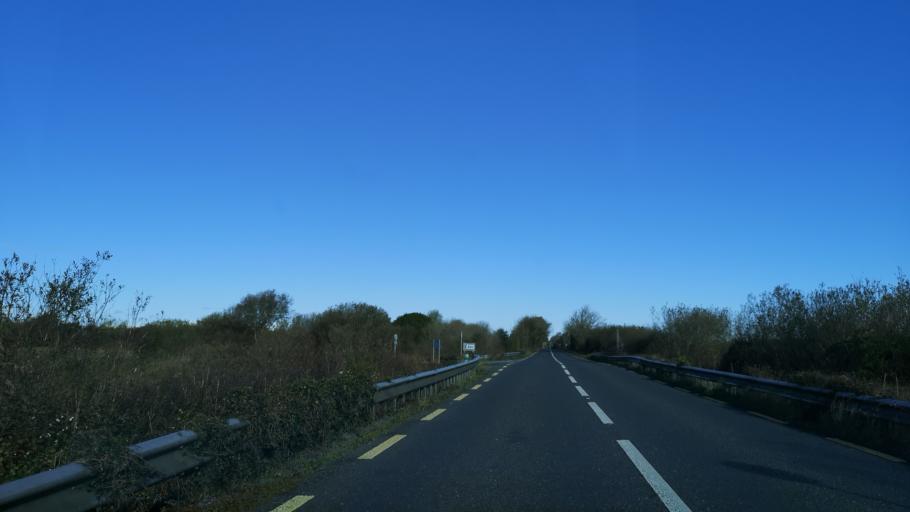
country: IE
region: Connaught
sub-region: County Galway
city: Claregalway
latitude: 53.3850
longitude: -9.0165
